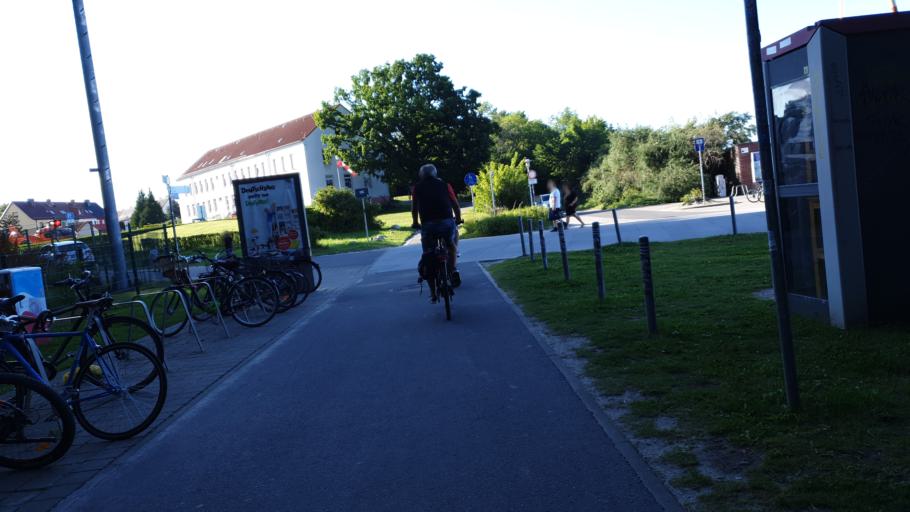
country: DE
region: Mecklenburg-Vorpommern
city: Stralsund
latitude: 54.3295
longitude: 13.0825
